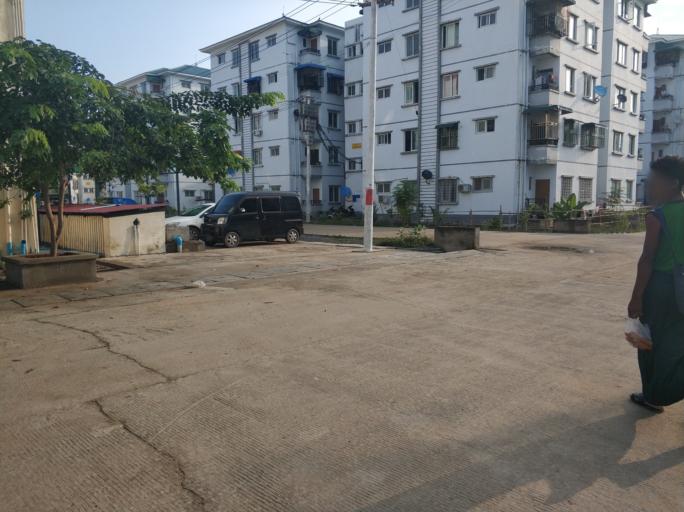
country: MM
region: Mandalay
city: Mandalay
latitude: 21.9159
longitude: 96.1342
